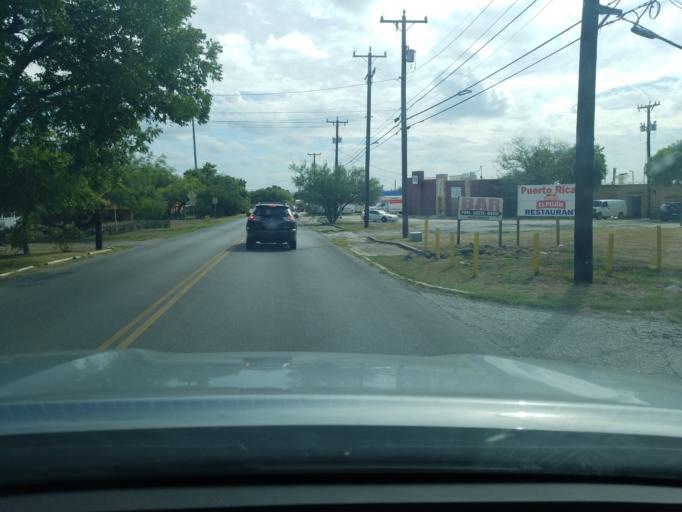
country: US
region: Texas
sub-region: Bexar County
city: Terrell Hills
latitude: 29.4703
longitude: -98.4395
